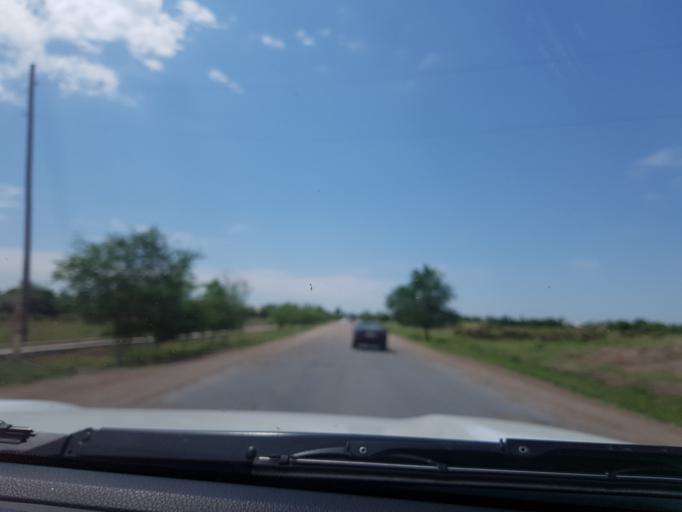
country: TM
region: Dasoguz
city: Koeneuergench
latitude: 42.3204
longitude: 59.1401
